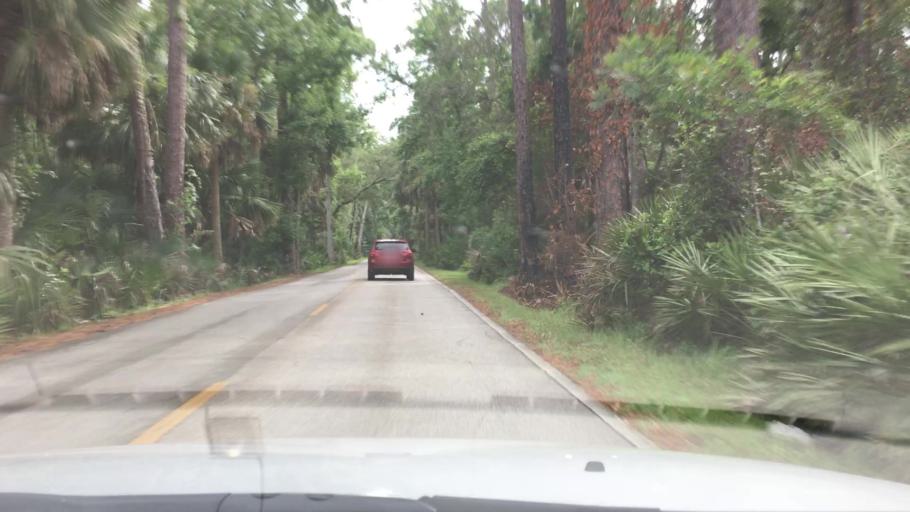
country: US
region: Florida
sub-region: Volusia County
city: Ormond-by-the-Sea
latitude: 29.3395
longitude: -81.1031
